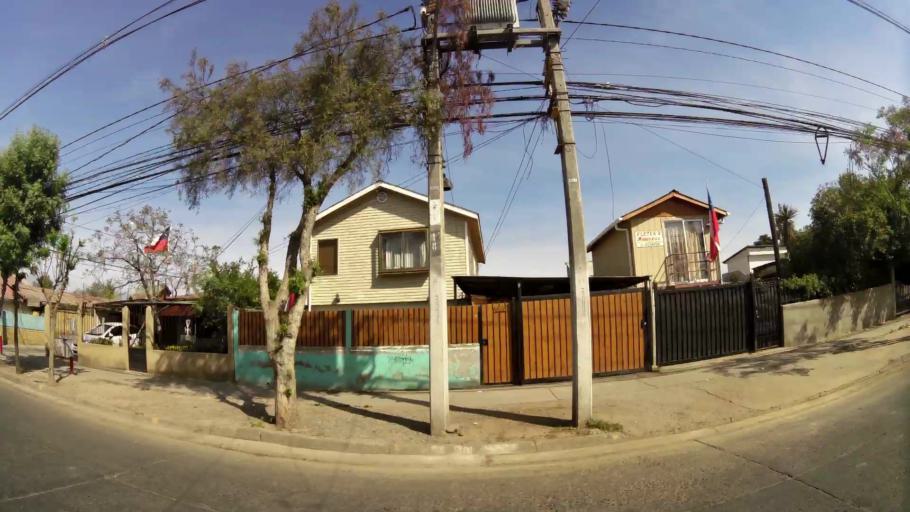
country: CL
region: Santiago Metropolitan
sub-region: Provincia de Santiago
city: La Pintana
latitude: -33.5356
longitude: -70.6025
